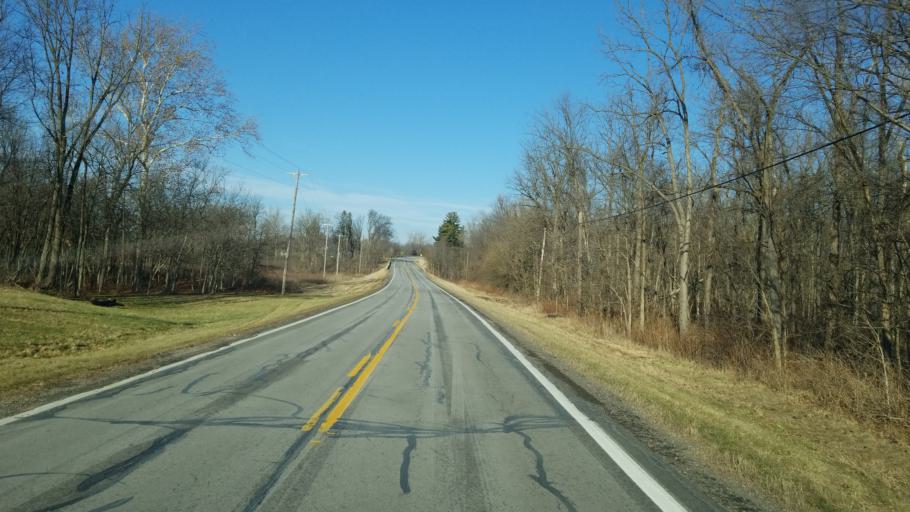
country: US
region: Ohio
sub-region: Huron County
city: Willard
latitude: 41.0973
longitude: -82.6611
